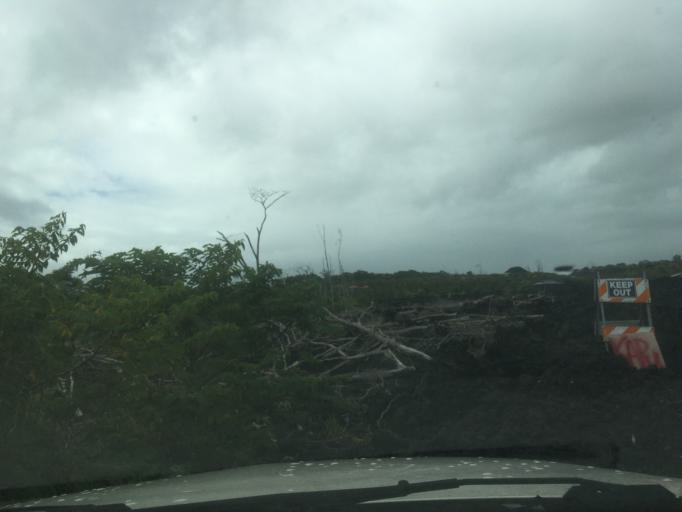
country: US
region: Hawaii
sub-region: Hawaii County
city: Leilani Estates
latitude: 19.4733
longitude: -154.8725
